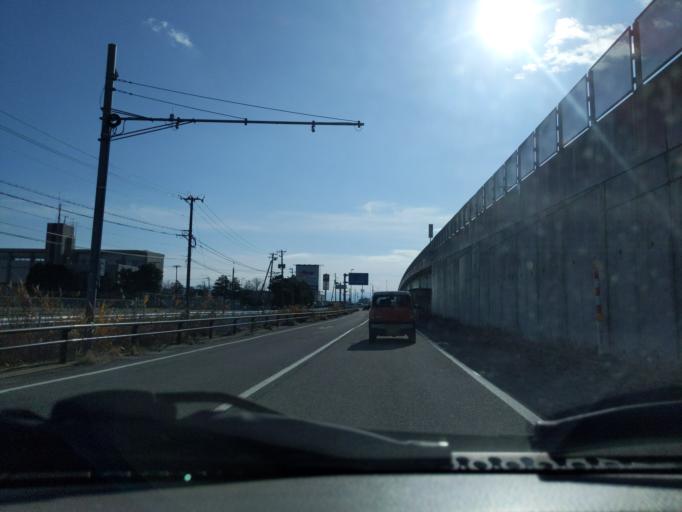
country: JP
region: Niigata
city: Kameda-honcho
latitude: 37.8712
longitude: 139.0871
